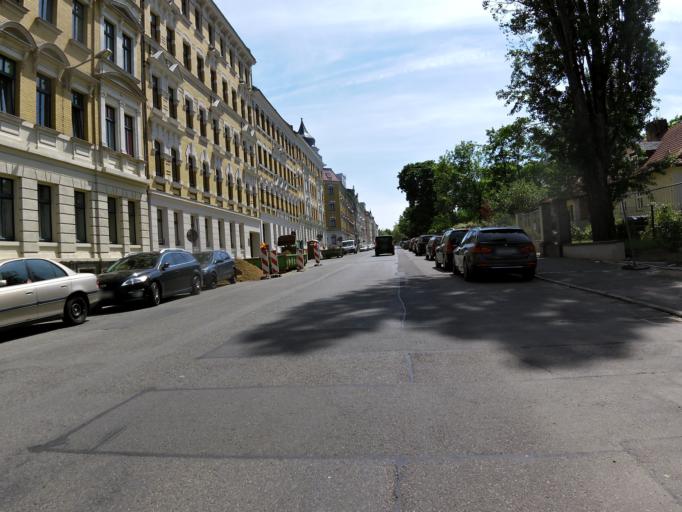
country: DE
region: Saxony
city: Leipzig
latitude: 51.3226
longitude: 12.4133
